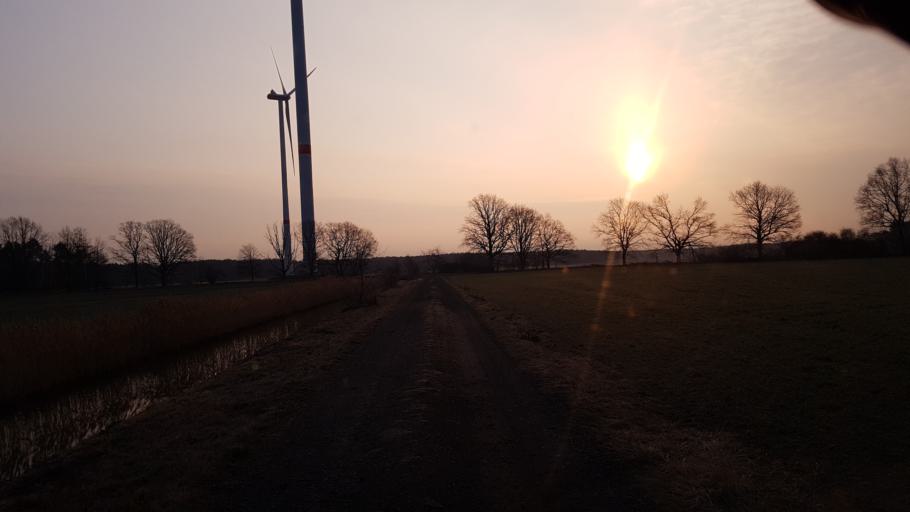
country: DE
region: Brandenburg
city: Falkenberg
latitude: 51.5720
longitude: 13.3048
